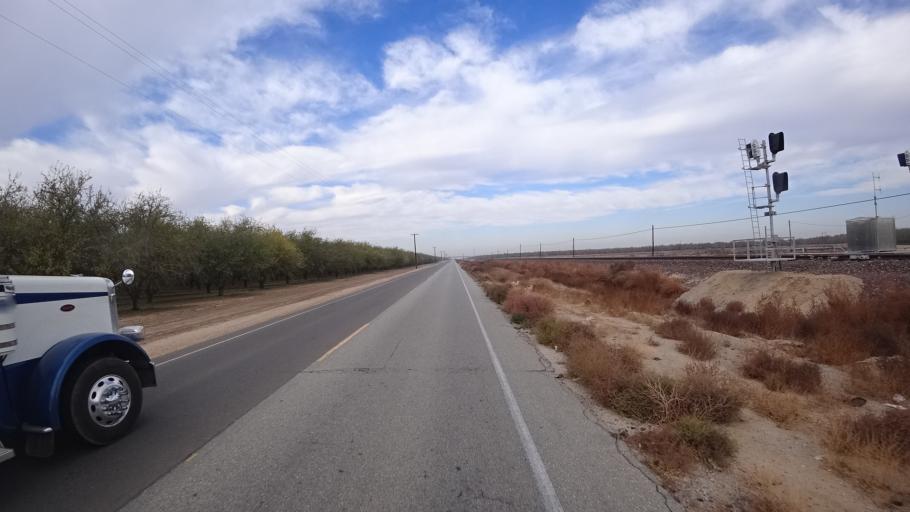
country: US
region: California
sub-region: Kern County
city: Rosedale
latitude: 35.4307
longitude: -119.1858
